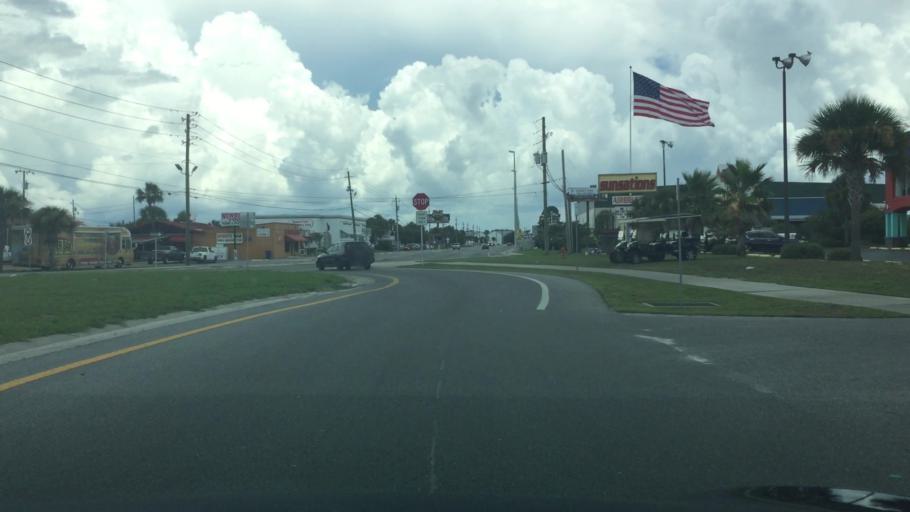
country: US
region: Florida
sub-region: Bay County
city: Lower Grand Lagoon
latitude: 30.1393
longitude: -85.7494
